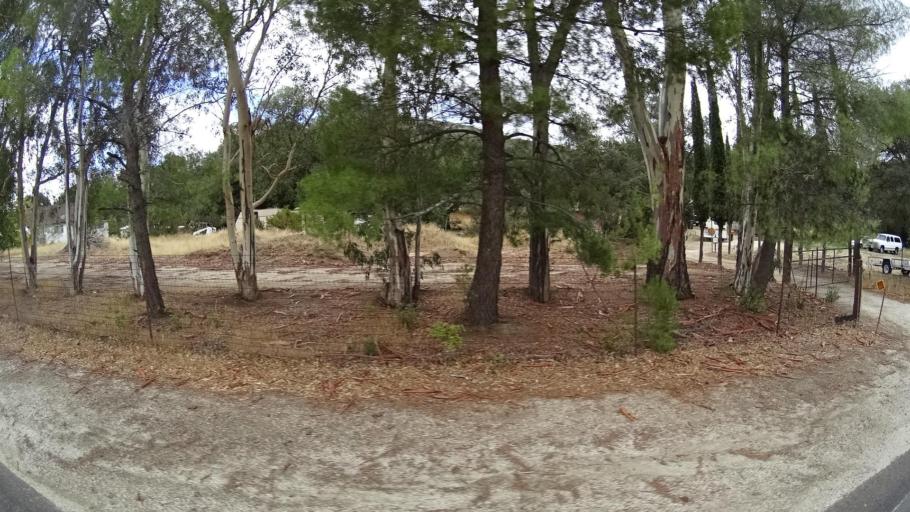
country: US
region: California
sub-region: San Diego County
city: Campo
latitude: 32.6589
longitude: -116.4986
